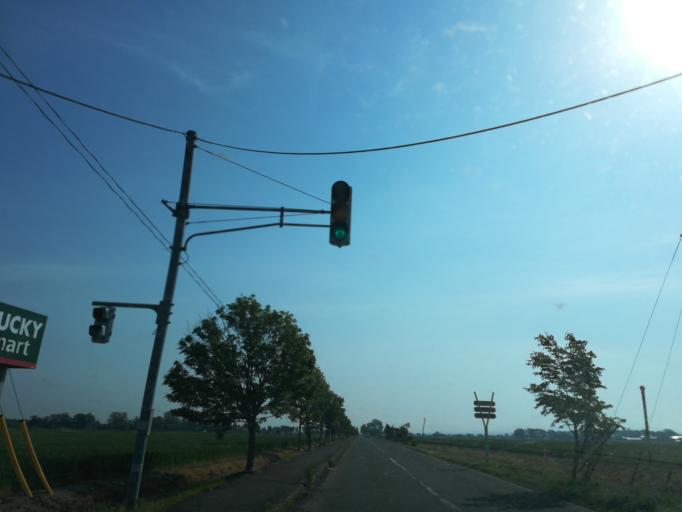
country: JP
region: Hokkaido
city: Iwamizawa
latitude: 43.1504
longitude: 141.6658
